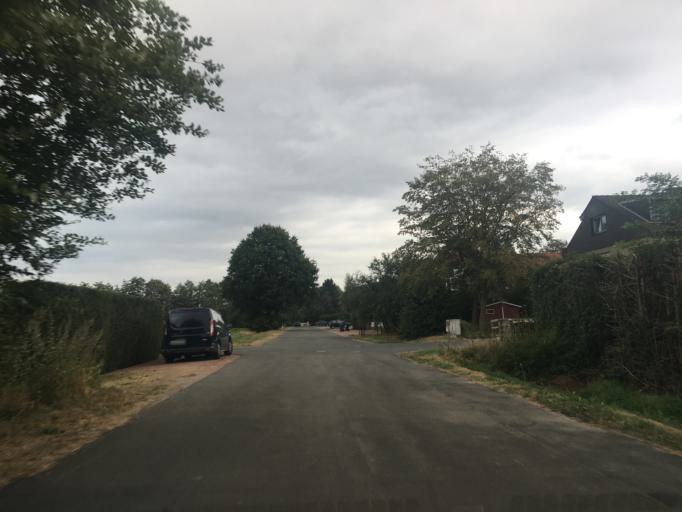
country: DE
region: North Rhine-Westphalia
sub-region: Regierungsbezirk Munster
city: Muenster
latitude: 51.9519
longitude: 7.5490
